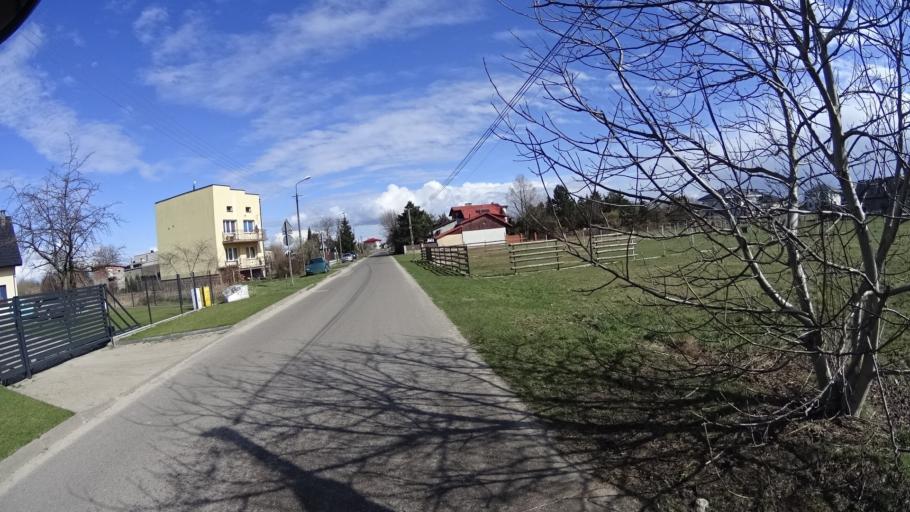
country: PL
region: Masovian Voivodeship
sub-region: Powiat warszawski zachodni
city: Jozefow
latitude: 52.2070
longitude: 20.6943
